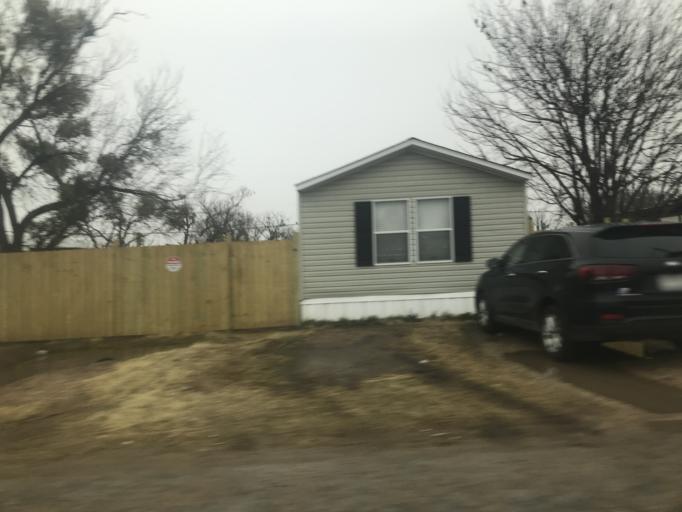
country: US
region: Texas
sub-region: Taylor County
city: Tye
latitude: 32.4448
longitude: -99.8116
